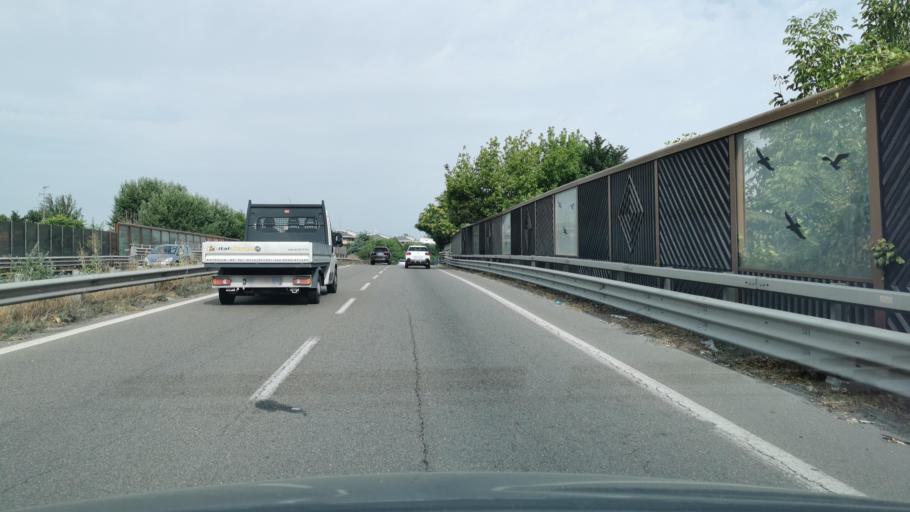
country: IT
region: Emilia-Romagna
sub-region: Provincia di Modena
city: Modena
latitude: 44.6601
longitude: 10.9474
